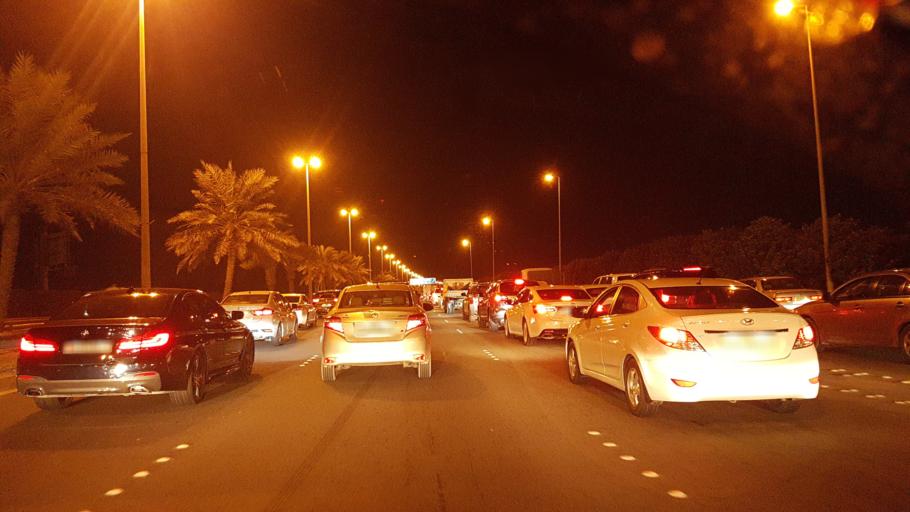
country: BH
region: Northern
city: Madinat `Isa
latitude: 26.1676
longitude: 50.5032
